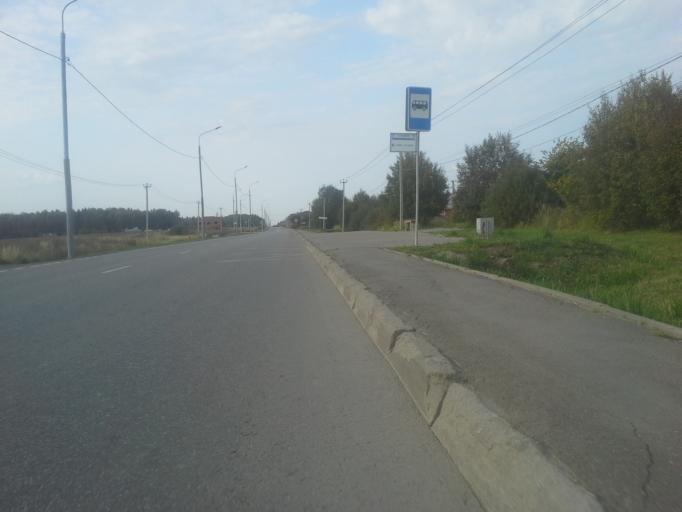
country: RU
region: Moskovskaya
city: Selyatino
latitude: 55.4312
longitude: 36.9608
